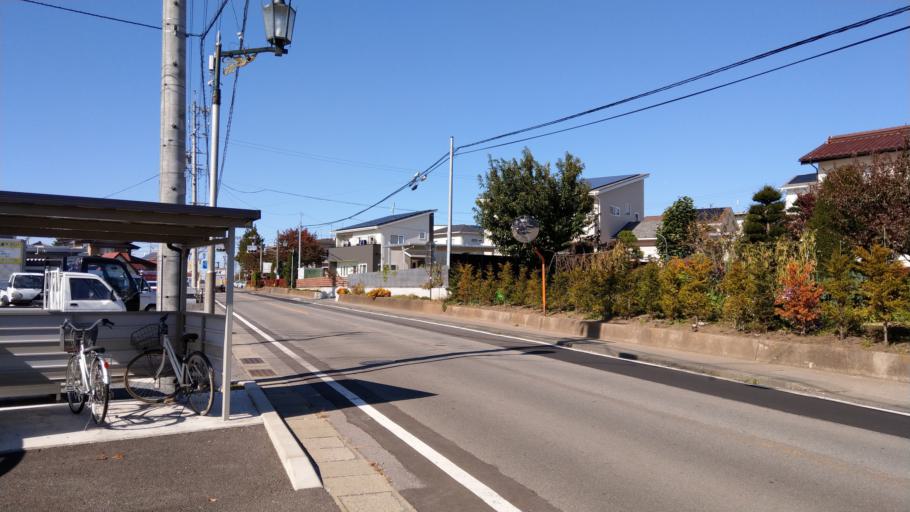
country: JP
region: Nagano
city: Komoro
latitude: 36.2845
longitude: 138.4642
